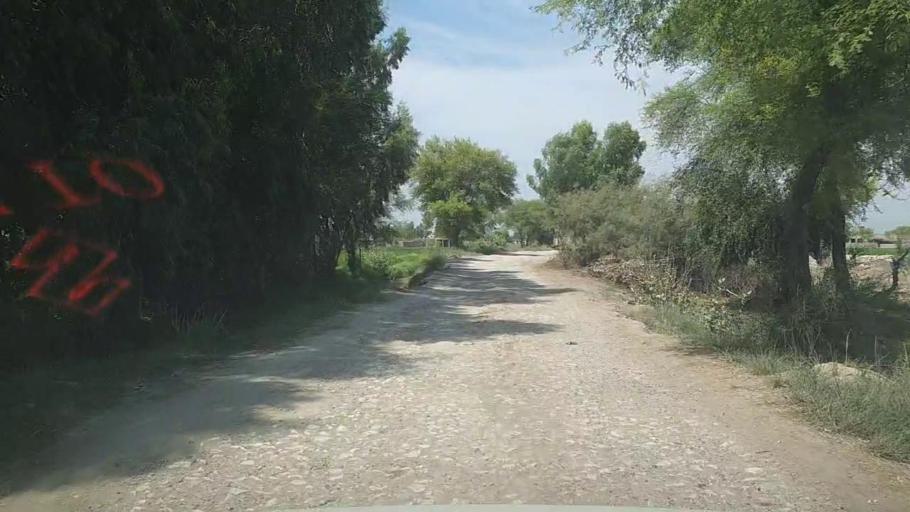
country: PK
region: Sindh
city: Kandhkot
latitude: 28.2767
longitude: 69.2353
